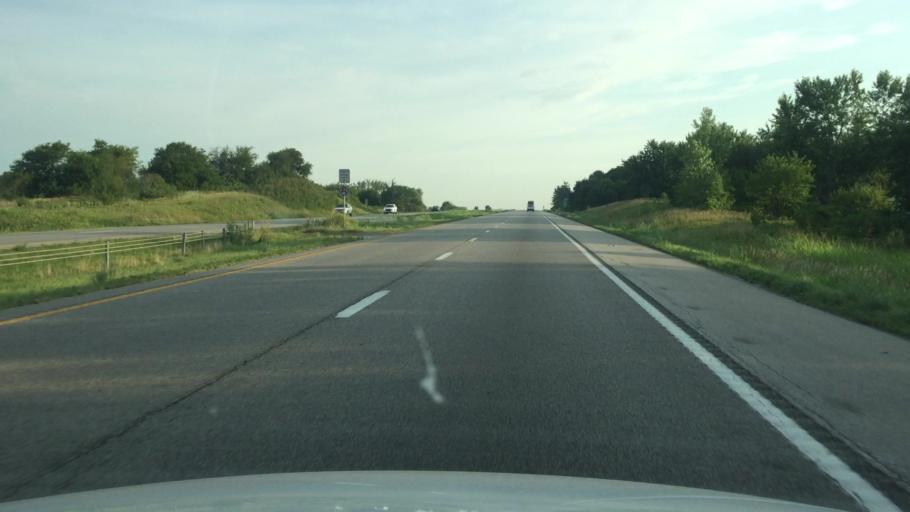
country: US
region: Missouri
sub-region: Buchanan County
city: Saint Joseph
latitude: 39.6343
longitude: -94.7879
